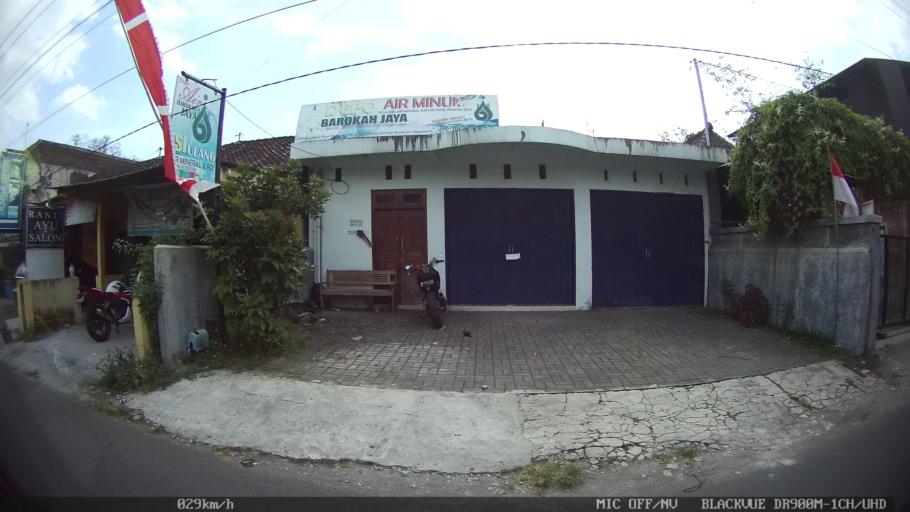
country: ID
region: Daerah Istimewa Yogyakarta
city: Gamping Lor
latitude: -7.8048
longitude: 110.3327
